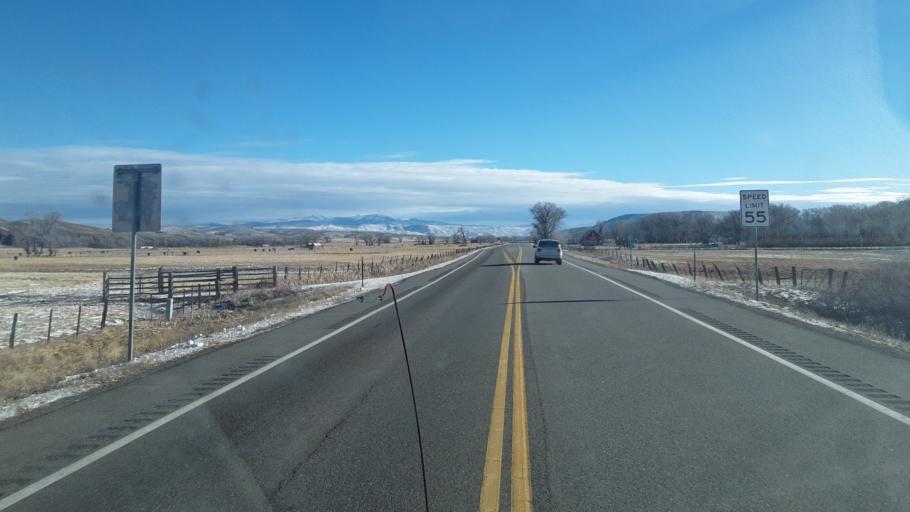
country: US
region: Colorado
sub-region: Gunnison County
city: Gunnison
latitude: 38.5208
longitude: -106.9985
